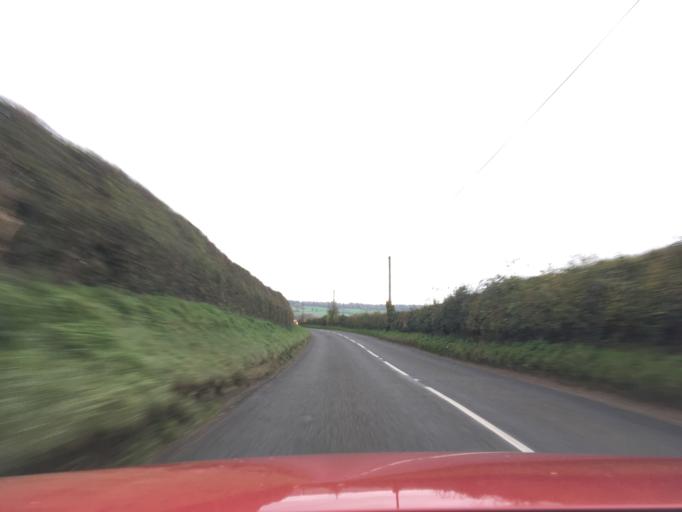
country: GB
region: England
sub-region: Dorset
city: Sherborne
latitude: 50.9603
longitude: -2.5438
